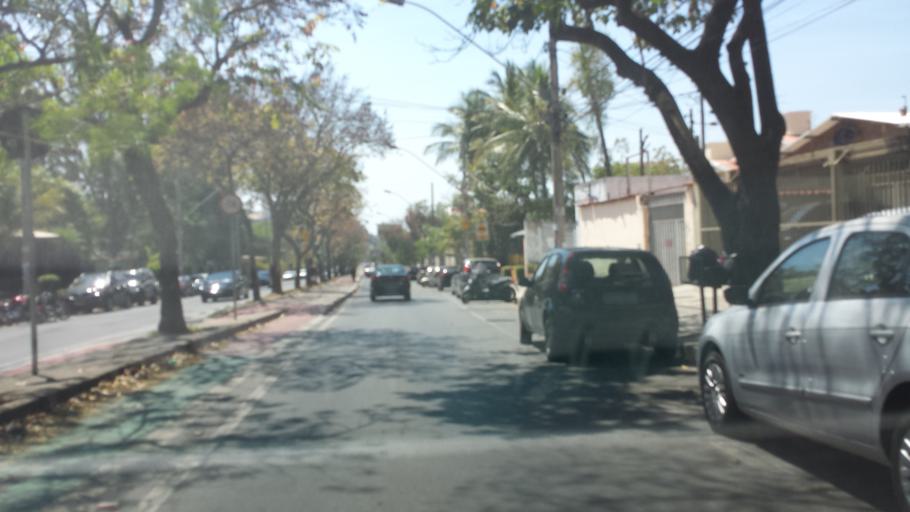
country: BR
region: Minas Gerais
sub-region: Belo Horizonte
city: Belo Horizonte
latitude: -19.8719
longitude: -43.9869
